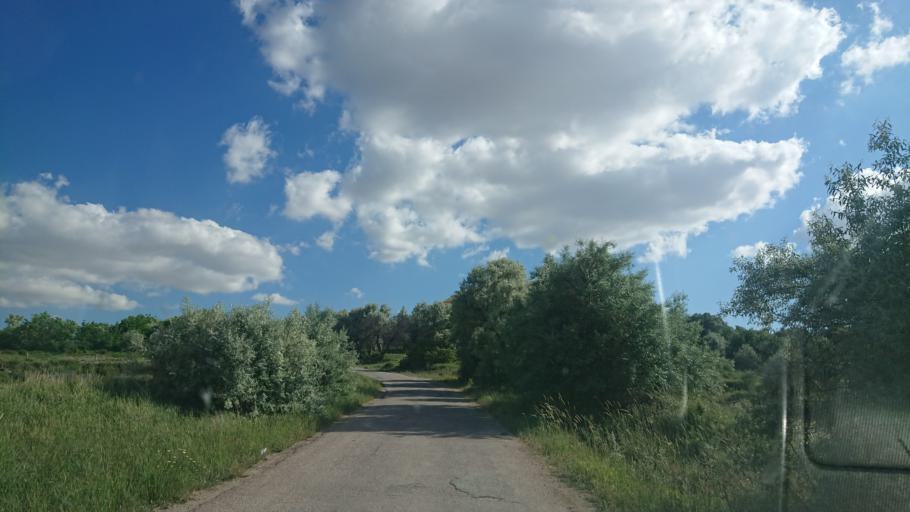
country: TR
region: Aksaray
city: Agacoren
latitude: 38.7566
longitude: 33.8873
